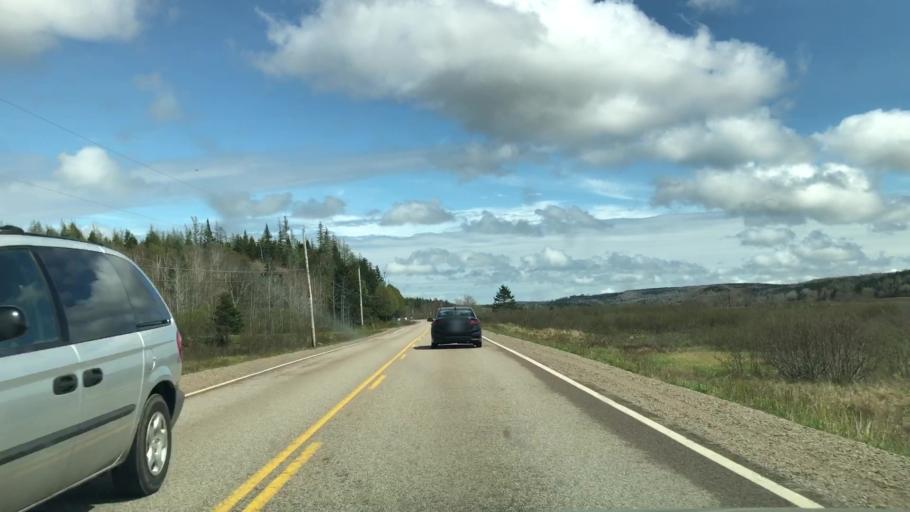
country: CA
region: Nova Scotia
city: Antigonish
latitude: 45.1948
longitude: -61.9990
